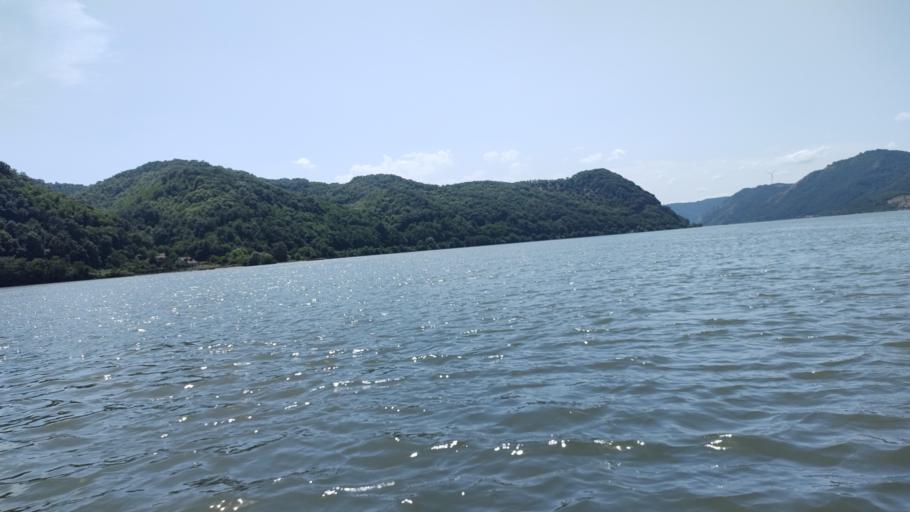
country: RS
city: Radenka
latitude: 44.6589
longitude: 21.7934
